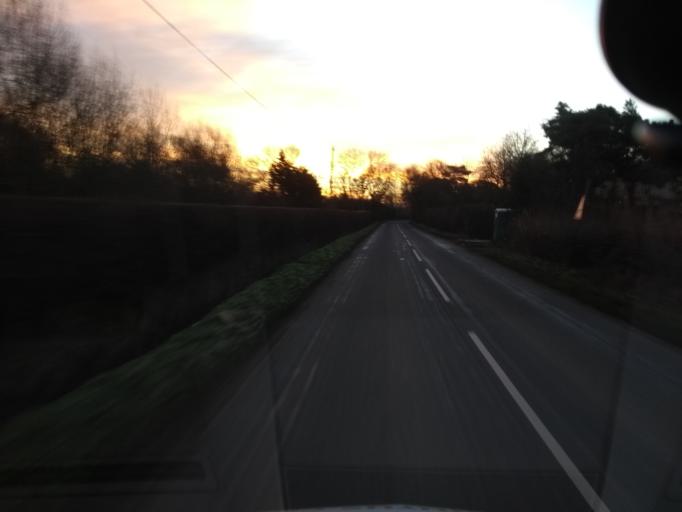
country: GB
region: England
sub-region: Somerset
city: Highbridge
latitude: 51.2243
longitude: -2.9388
